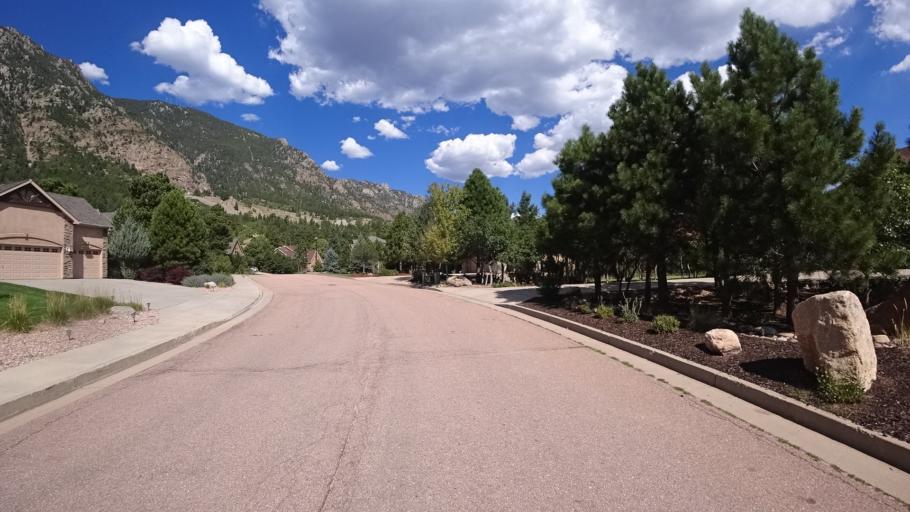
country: US
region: Colorado
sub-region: El Paso County
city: Fort Carson
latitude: 38.7424
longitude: -104.8381
